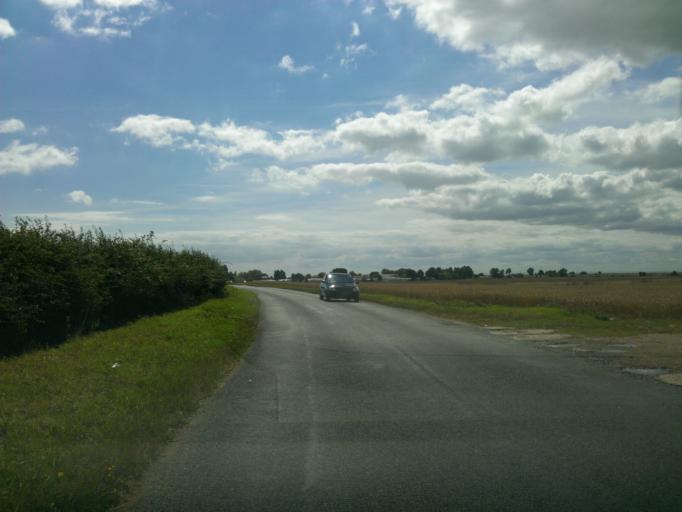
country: GB
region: England
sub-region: Essex
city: Saint Osyth
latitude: 51.7851
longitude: 1.0866
